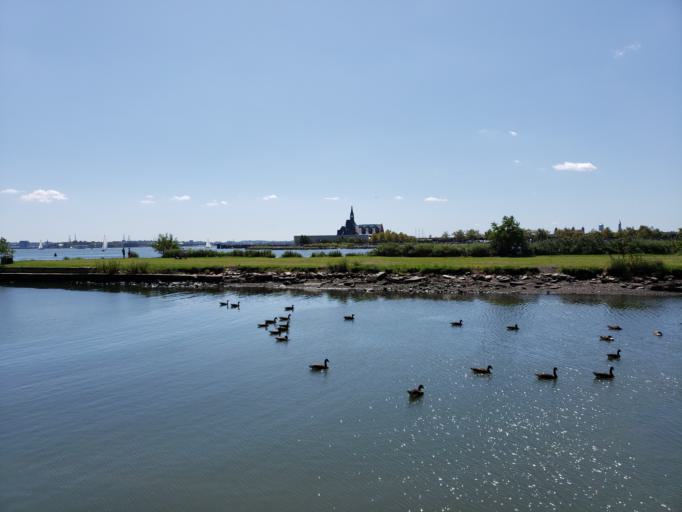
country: US
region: New York
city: New York City
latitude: 40.7122
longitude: -74.0361
